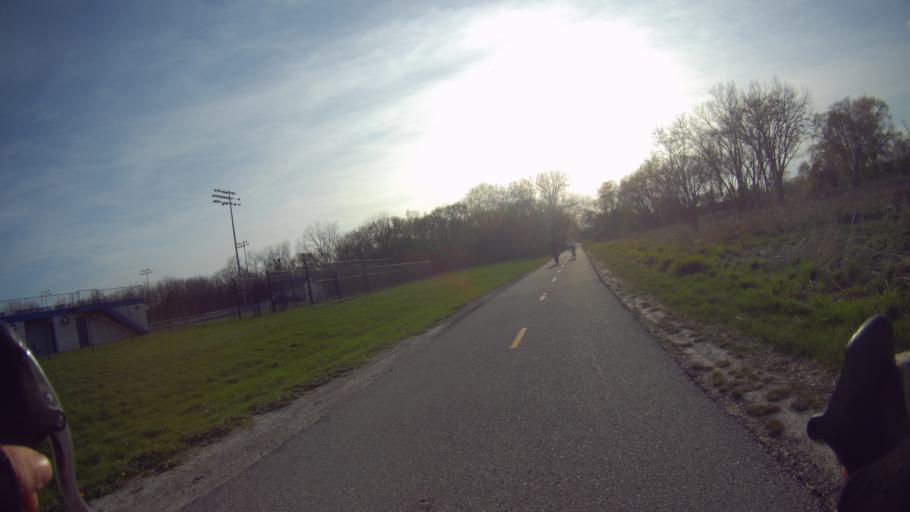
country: US
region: Wisconsin
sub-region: Dane County
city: Maple Bluff
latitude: 43.1173
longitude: -89.3350
